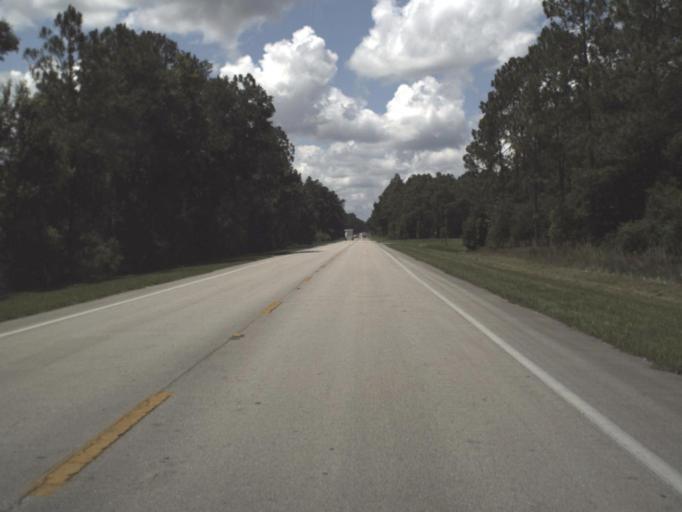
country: US
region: Florida
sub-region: Putnam County
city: Crescent City
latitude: 29.4021
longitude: -81.5093
